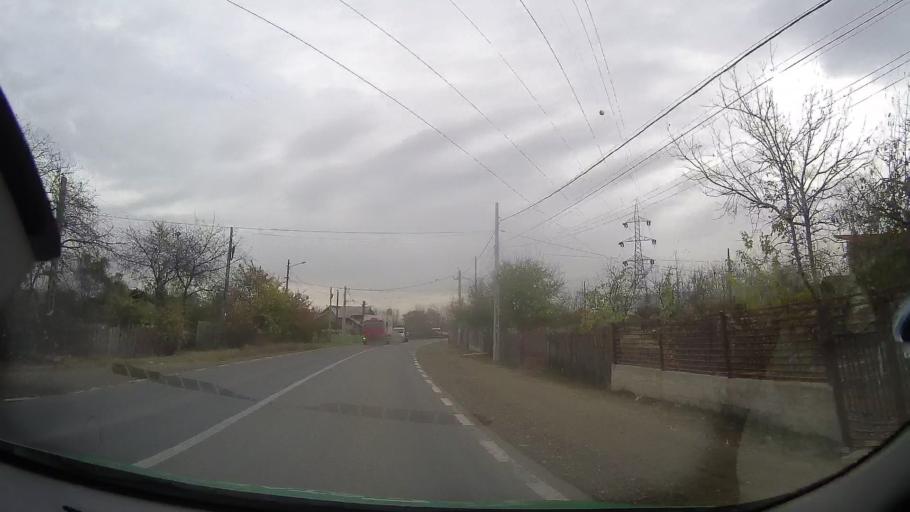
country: RO
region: Prahova
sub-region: Comuna Bucov
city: Bucov
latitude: 44.9488
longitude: 26.0979
